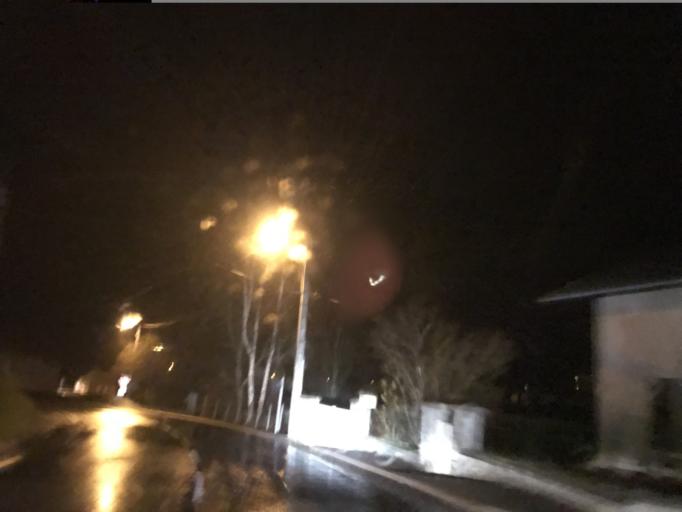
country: FR
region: Auvergne
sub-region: Departement du Puy-de-Dome
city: Celles-sur-Durolle
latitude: 45.8695
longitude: 3.6367
